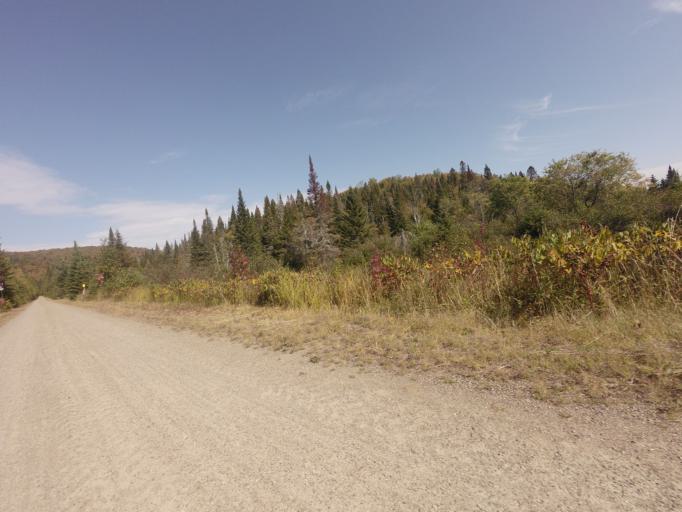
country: CA
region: Quebec
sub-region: Laurentides
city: Sainte-Agathe-des-Monts
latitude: 46.0993
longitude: -74.3632
